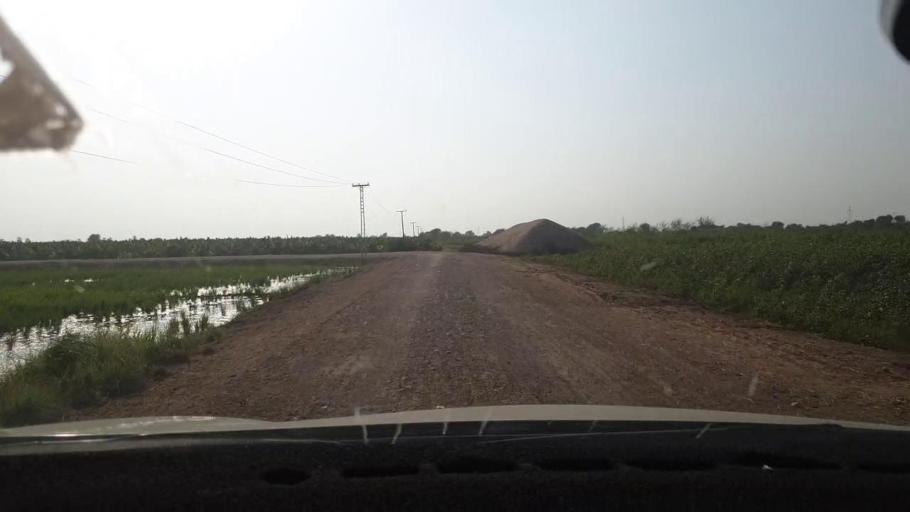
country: PK
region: Sindh
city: Berani
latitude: 25.7502
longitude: 68.7905
